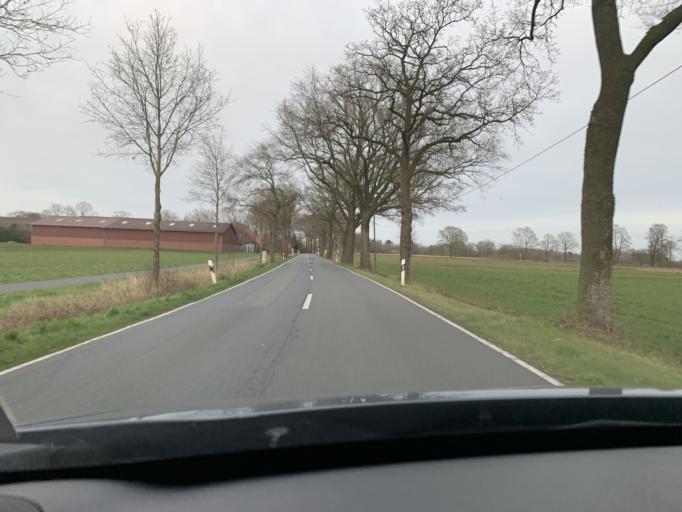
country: DE
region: Lower Saxony
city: Apen
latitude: 53.1767
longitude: 7.8086
